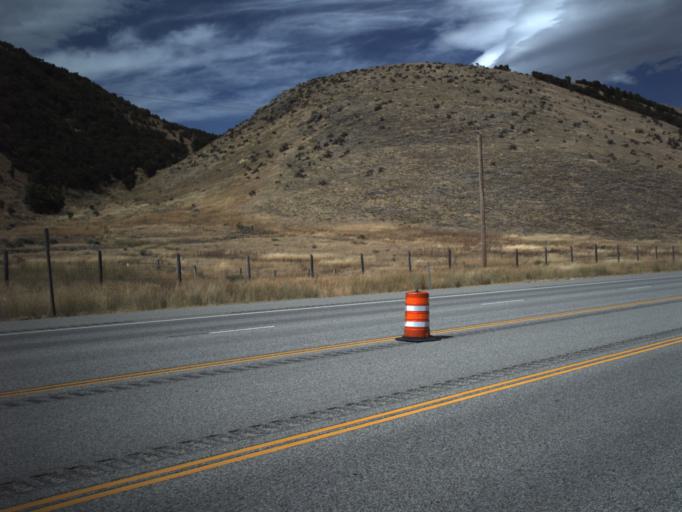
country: US
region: Utah
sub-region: Box Elder County
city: Brigham City
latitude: 41.5093
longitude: -111.9449
